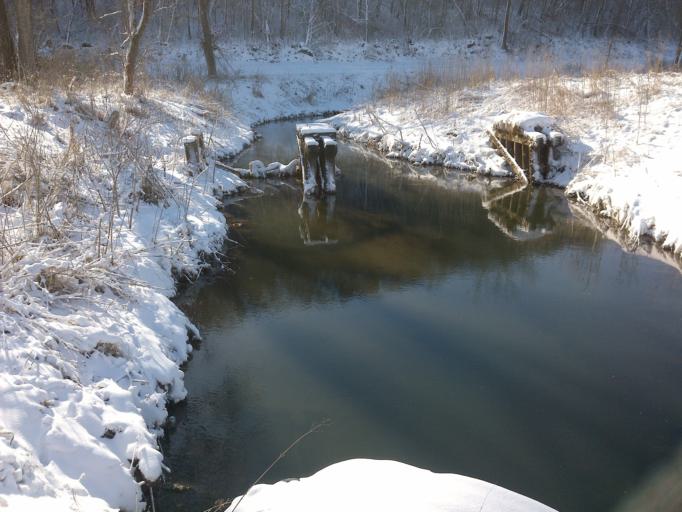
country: US
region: Minnesota
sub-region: Goodhue County
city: Goodhue
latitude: 44.4776
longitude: -92.5874
